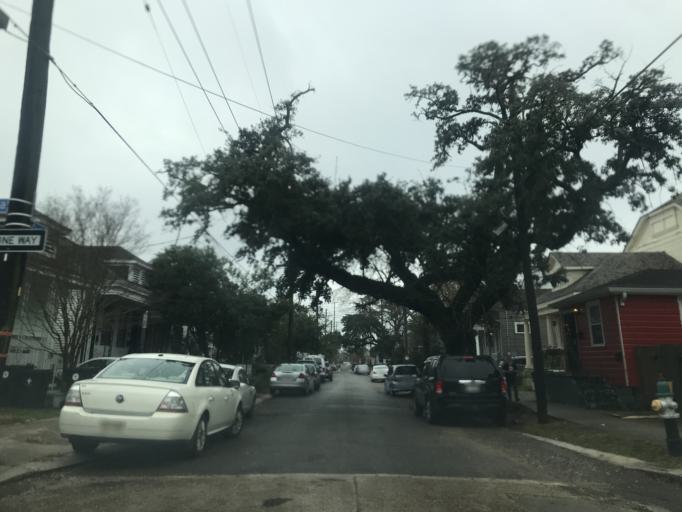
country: US
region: Louisiana
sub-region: Orleans Parish
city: New Orleans
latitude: 29.9708
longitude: -90.0992
